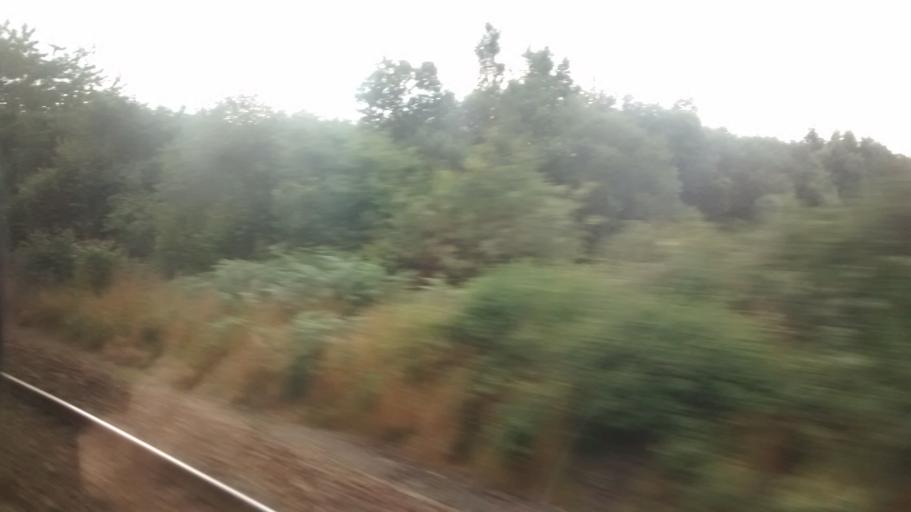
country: FR
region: Brittany
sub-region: Departement d'Ille-et-Vilaine
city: Cesson-Sevigne
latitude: 48.1204
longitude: -1.5714
